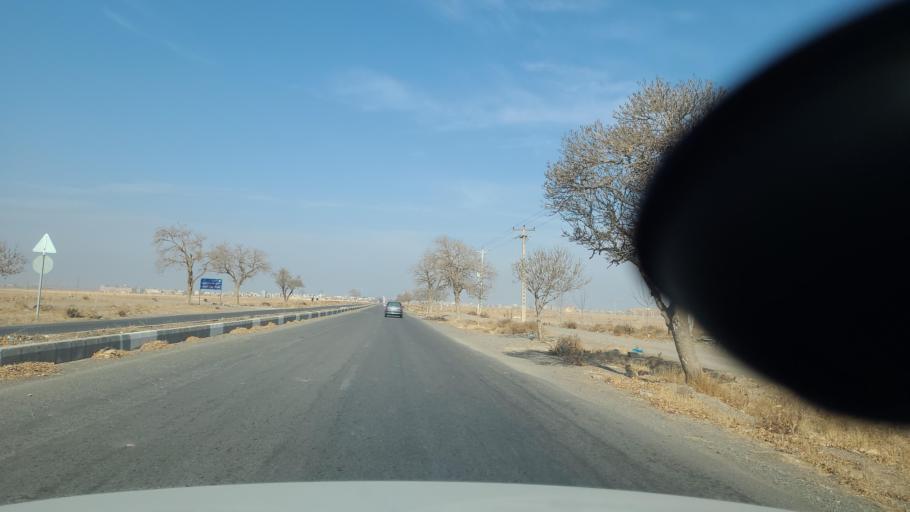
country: IR
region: Razavi Khorasan
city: Fariman
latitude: 35.6686
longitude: 59.8420
